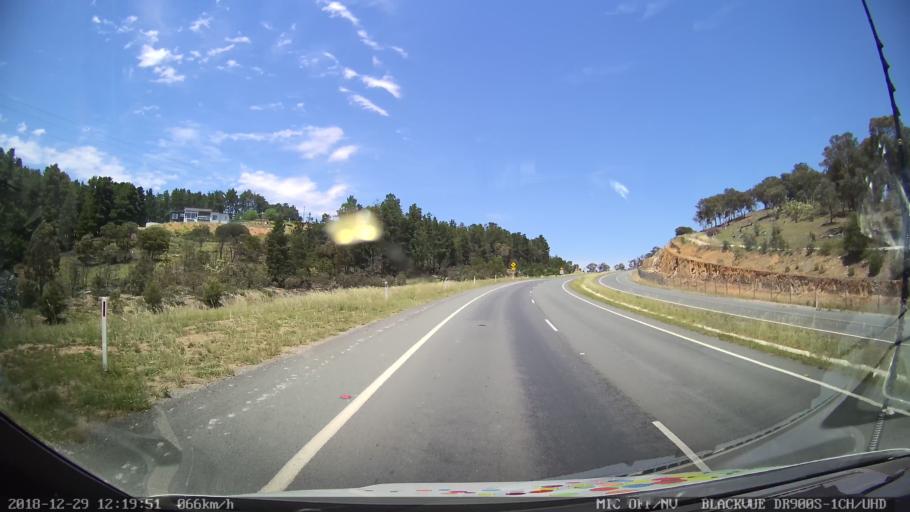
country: AU
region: New South Wales
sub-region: Queanbeyan
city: Queanbeyan
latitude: -35.3978
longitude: 149.2332
